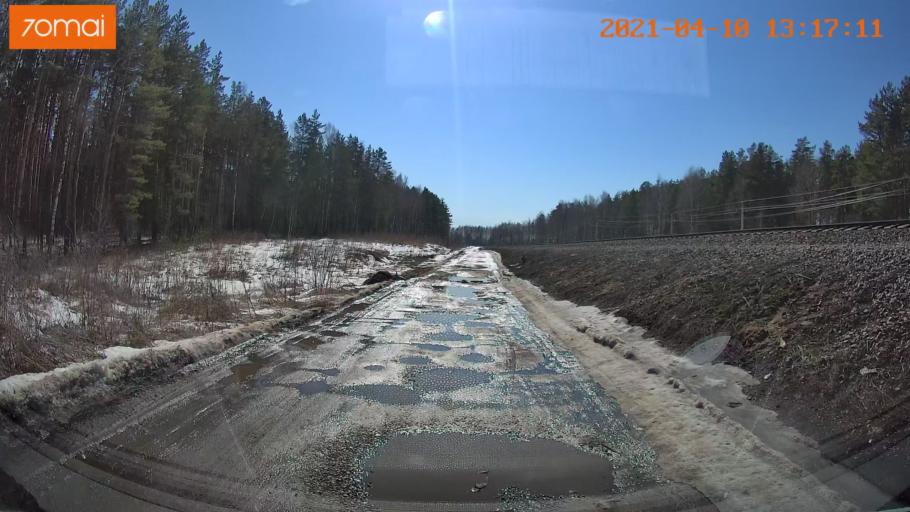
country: RU
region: Ivanovo
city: Kokhma
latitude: 56.9953
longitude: 41.0593
